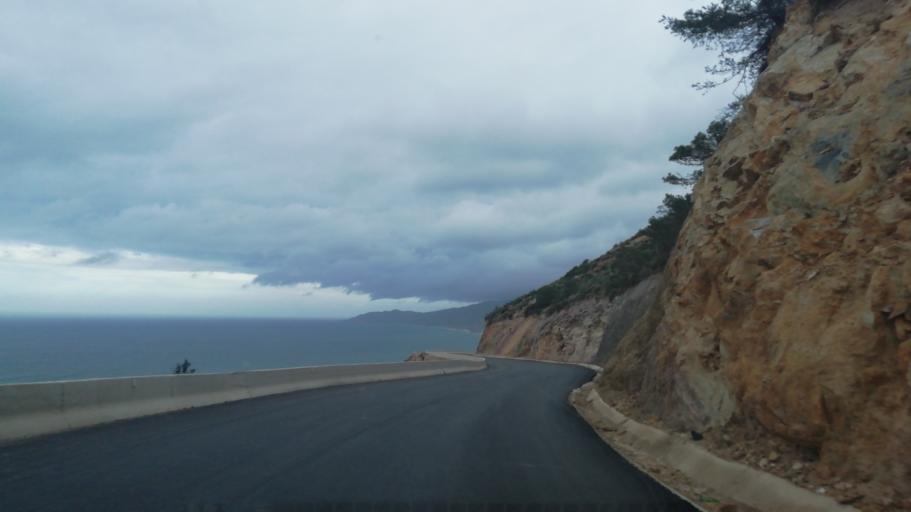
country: DZ
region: Oran
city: Bir el Djir
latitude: 35.7633
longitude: -0.5273
